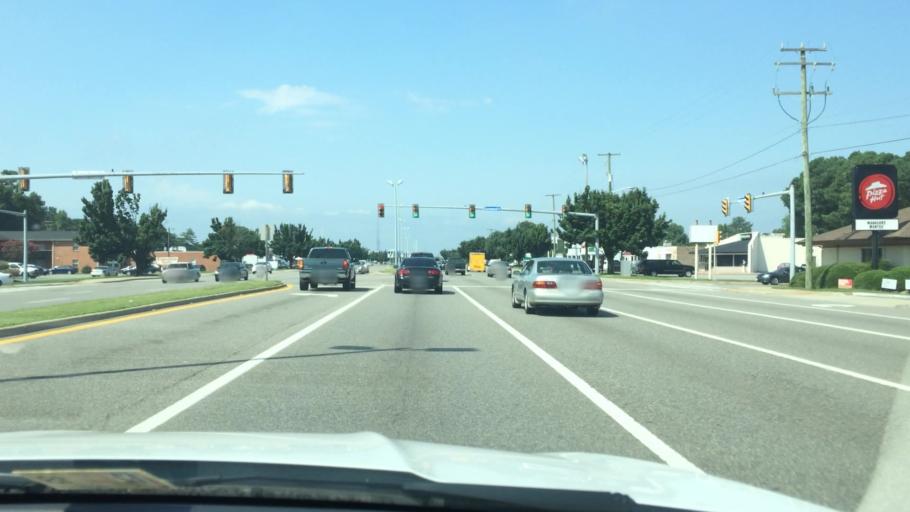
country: US
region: Virginia
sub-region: City of Newport News
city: Newport News
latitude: 37.0348
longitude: -76.4138
